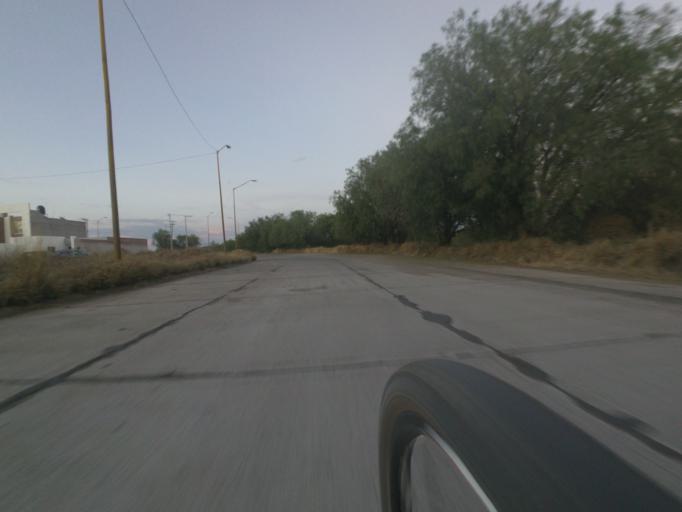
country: MX
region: Aguascalientes
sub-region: Aguascalientes
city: La Loma de los Negritos
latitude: 21.8493
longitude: -102.3297
